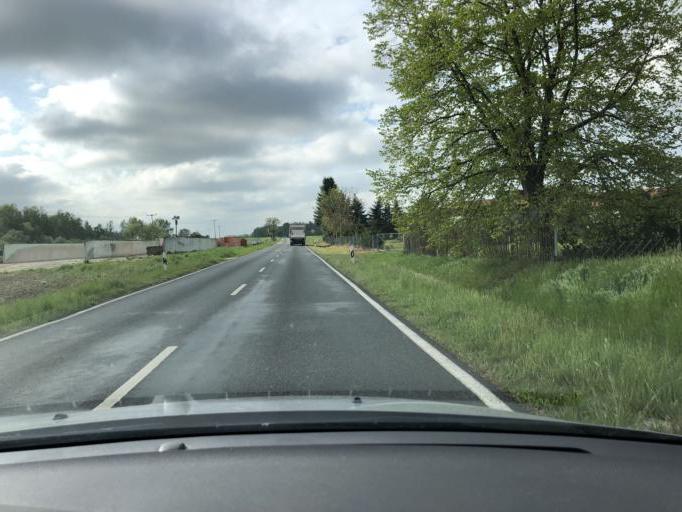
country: DE
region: Saxony
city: Deutzen
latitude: 51.1083
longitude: 12.4281
